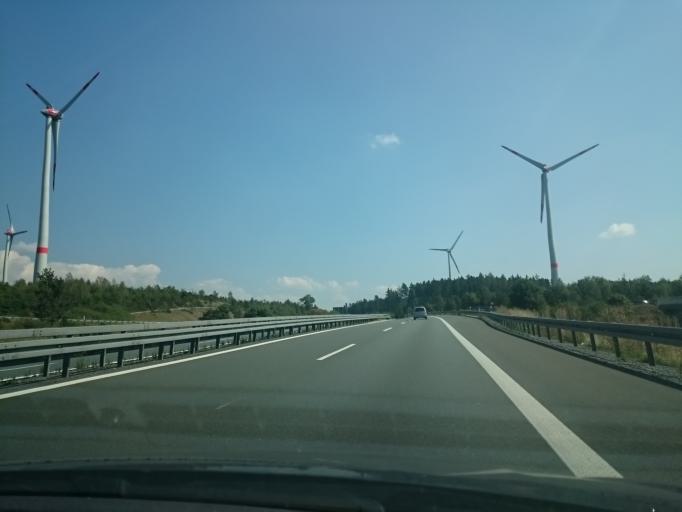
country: DE
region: Bavaria
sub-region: Upper Franconia
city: Trogen
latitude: 50.3841
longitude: 11.9641
